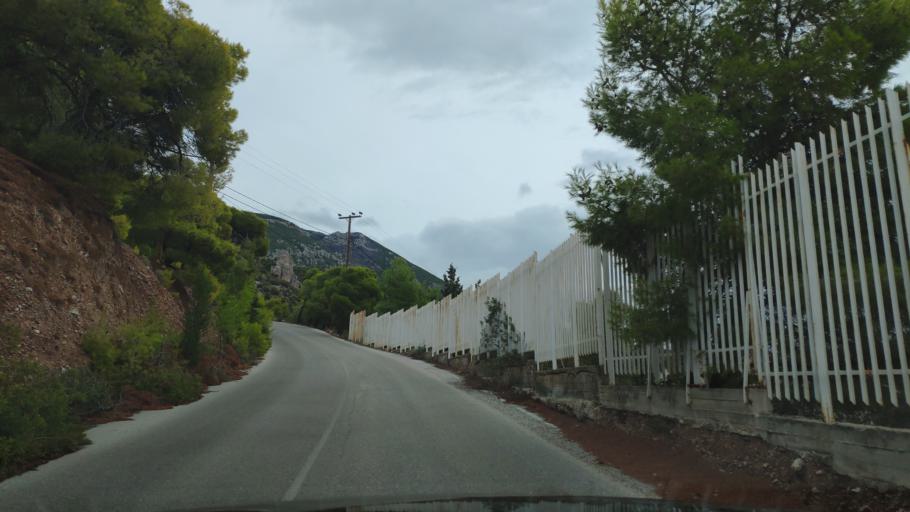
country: GR
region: Peloponnese
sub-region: Nomos Korinthias
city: Perachora
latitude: 38.0028
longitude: 22.9358
